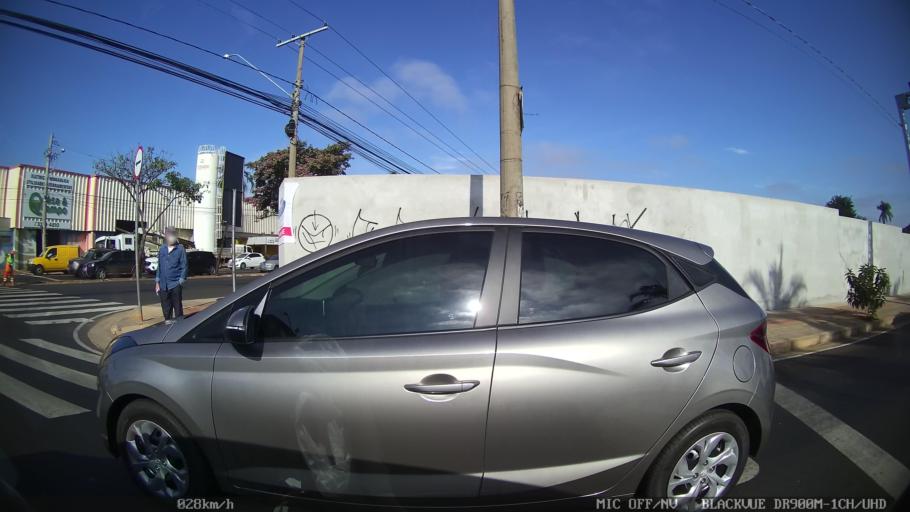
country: BR
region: Sao Paulo
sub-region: Sao Jose Do Rio Preto
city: Sao Jose do Rio Preto
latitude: -20.8092
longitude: -49.3995
